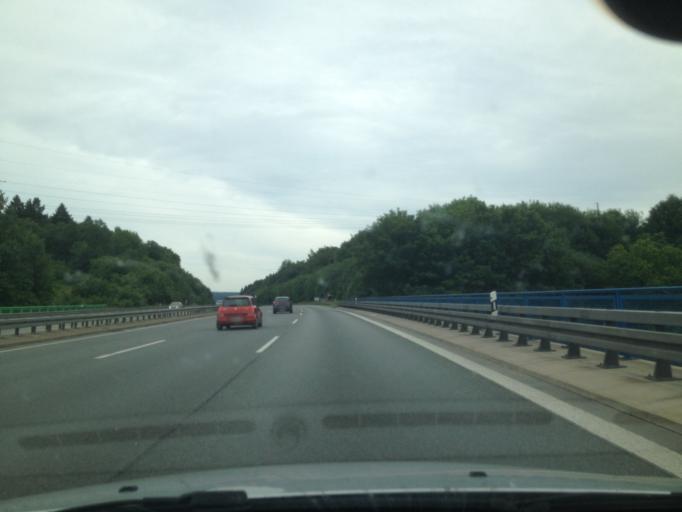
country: DE
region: North Rhine-Westphalia
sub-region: Regierungsbezirk Arnsberg
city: Luedenscheid
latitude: 51.2141
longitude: 7.6689
